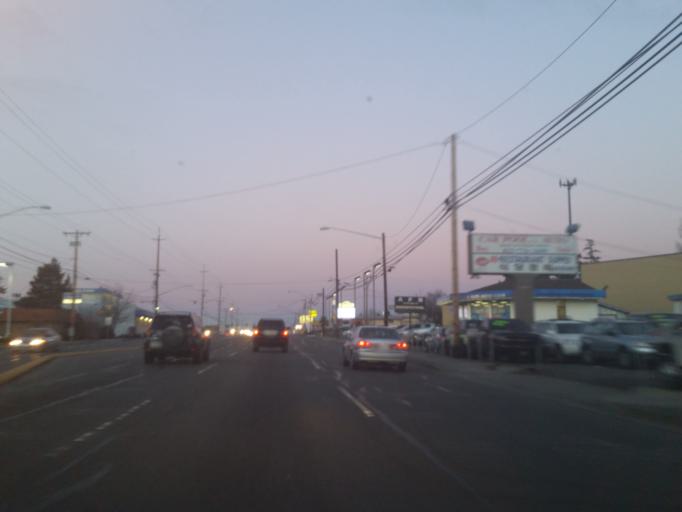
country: US
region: Washington
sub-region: Snohomish County
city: Lynnwood
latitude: 47.8147
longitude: -122.3206
